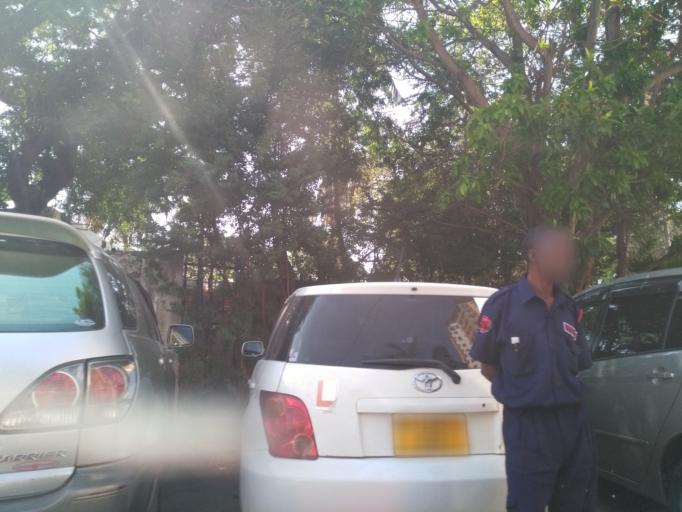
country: TZ
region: Dar es Salaam
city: Dar es Salaam
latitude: -6.8102
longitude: 39.2807
